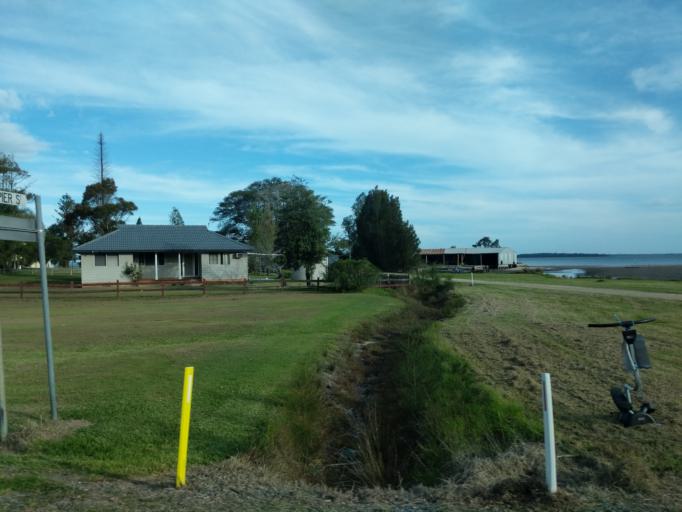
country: AU
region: New South Wales
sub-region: Port Stephens Shire
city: Port Stephens
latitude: -32.6669
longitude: 152.0132
